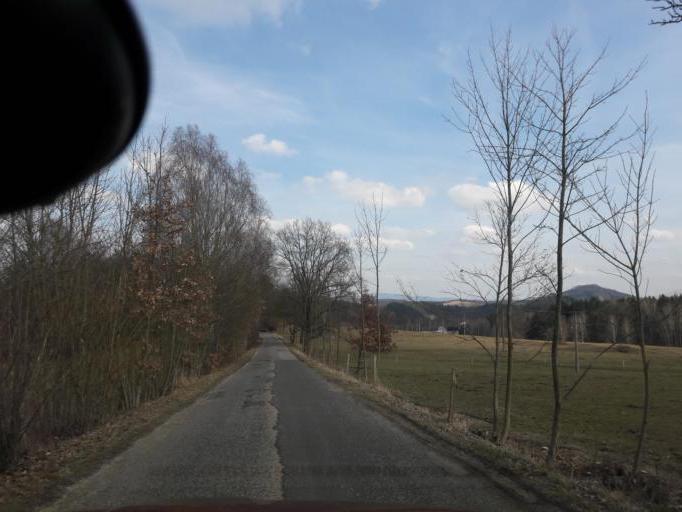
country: CZ
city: Cvikov
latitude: 50.7295
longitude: 14.6219
